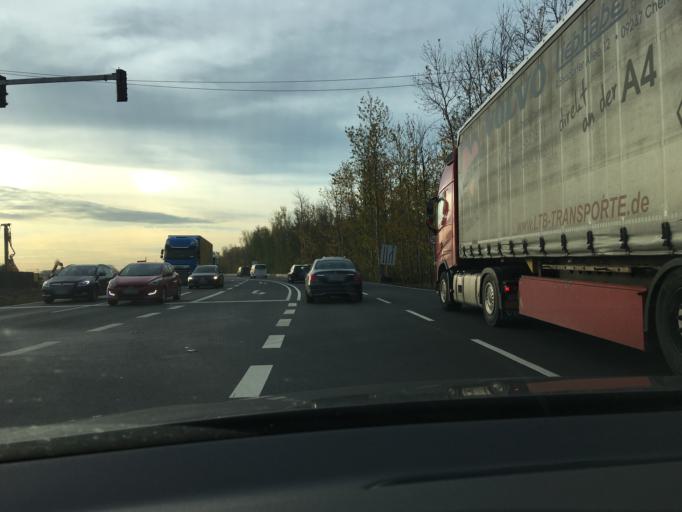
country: DE
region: Saxony
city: Bohlen
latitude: 51.2153
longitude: 12.3887
